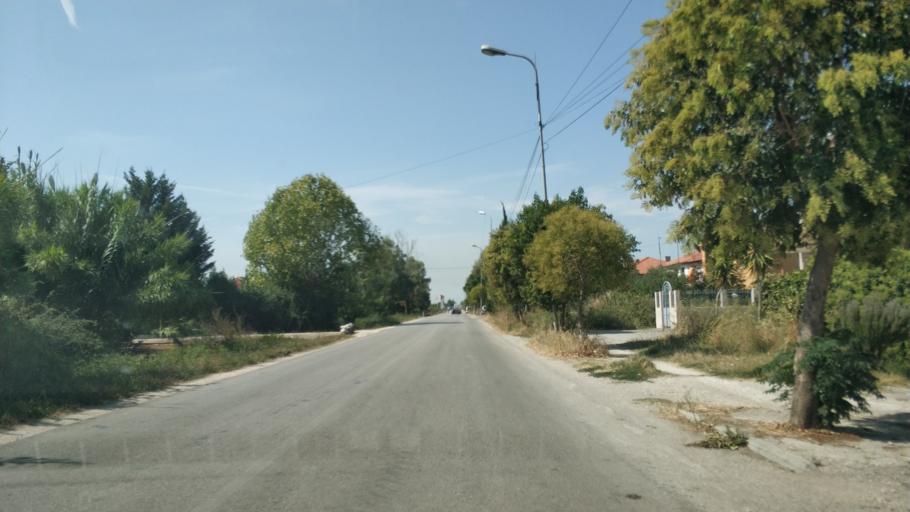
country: AL
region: Fier
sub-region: Rrethi i Fierit
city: Dermenas
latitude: 40.7366
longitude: 19.5213
